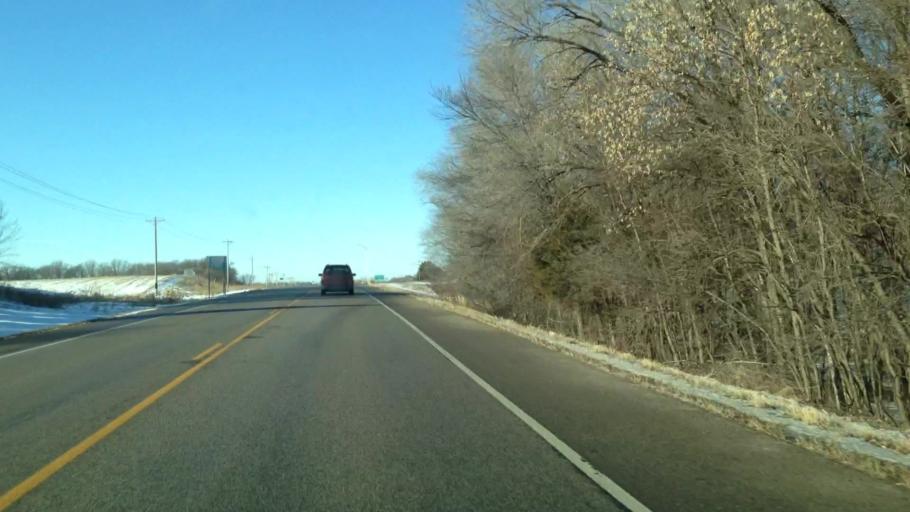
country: US
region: Minnesota
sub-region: Le Sueur County
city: New Prague
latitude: 44.5438
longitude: -93.4953
